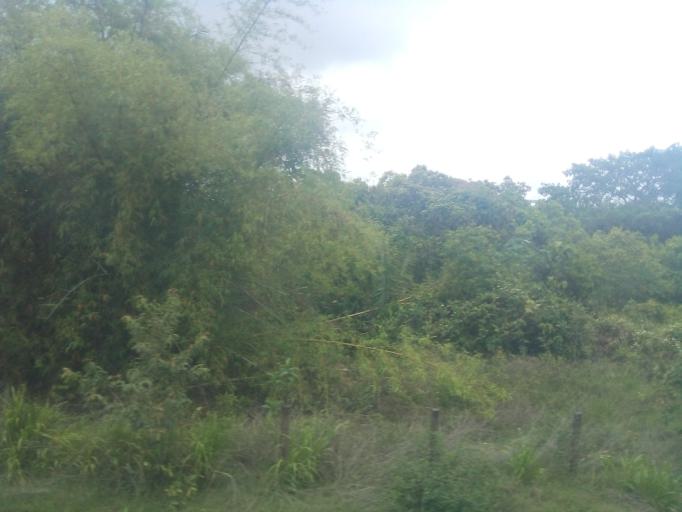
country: BR
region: Maranhao
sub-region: Vitoria Do Mearim
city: Vitoria do Mearim
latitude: -3.5505
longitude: -44.8264
